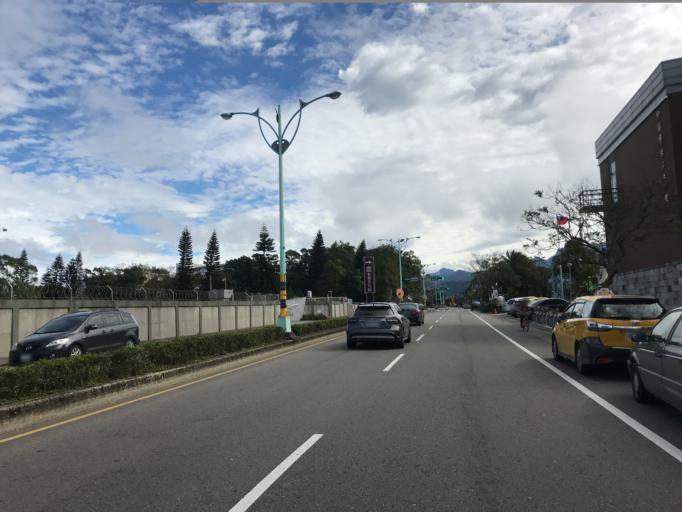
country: TW
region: Taiwan
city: Daxi
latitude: 24.8462
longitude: 121.2340
